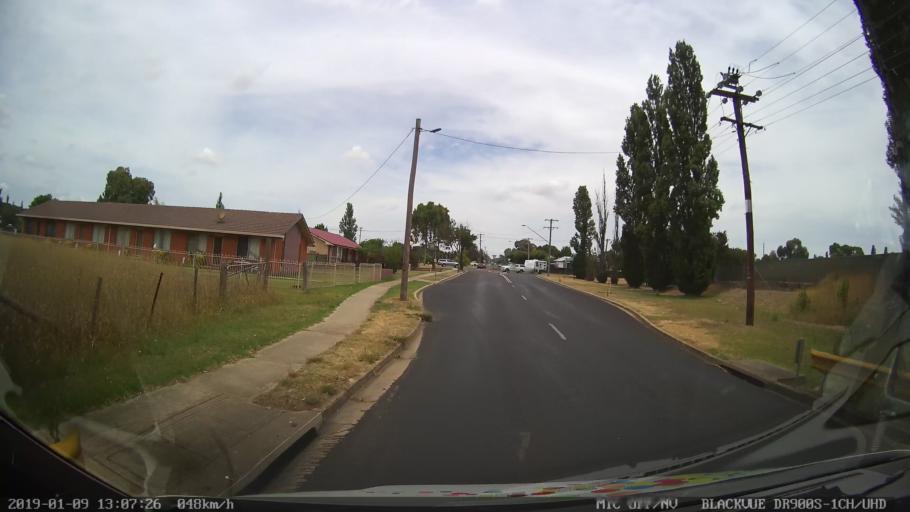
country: AU
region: New South Wales
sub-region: Armidale Dumaresq
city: Armidale
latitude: -30.5196
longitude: 151.6796
